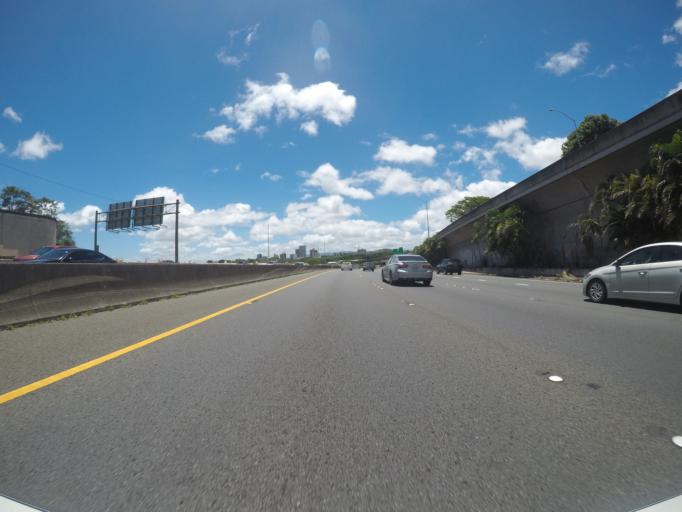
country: US
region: Hawaii
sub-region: Honolulu County
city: Halawa Heights
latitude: 21.3431
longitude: -157.8904
